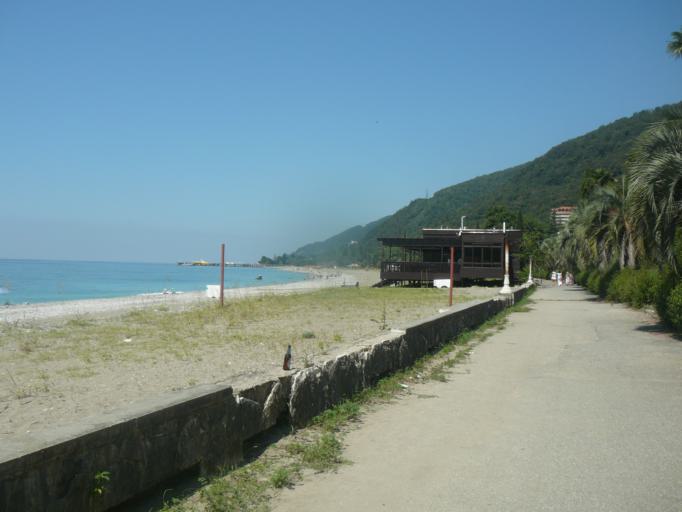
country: GE
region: Abkhazia
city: Gagra
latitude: 43.3196
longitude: 40.2402
